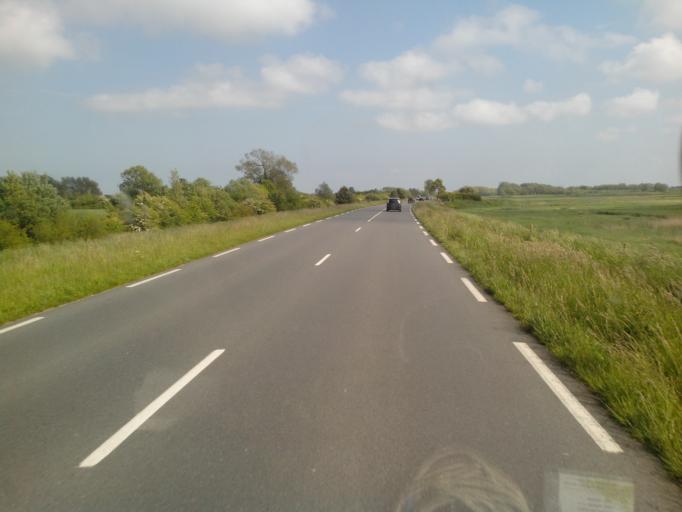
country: FR
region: Picardie
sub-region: Departement de la Somme
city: Saint-Valery-sur-Somme
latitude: 50.2060
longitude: 1.6820
